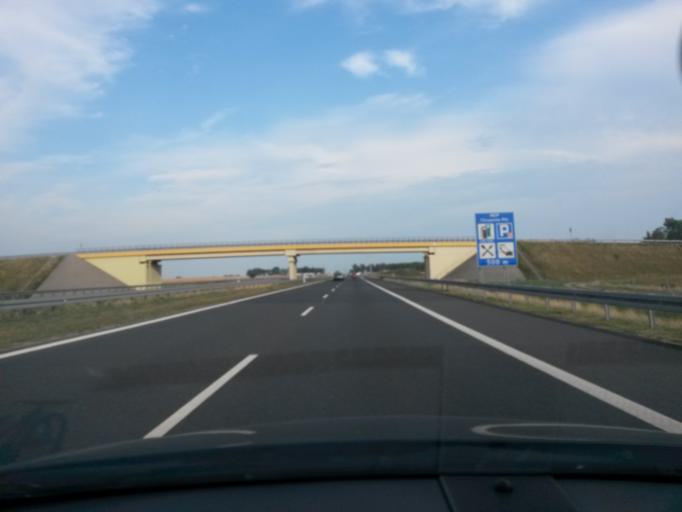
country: PL
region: Lodz Voivodeship
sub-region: Powiat zgierski
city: Parzeczew
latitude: 51.9490
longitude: 19.1646
